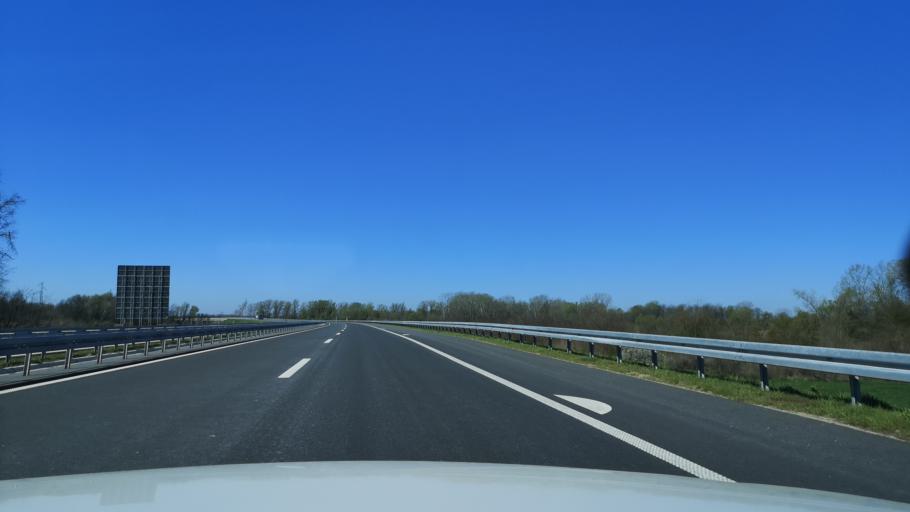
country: RS
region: Central Serbia
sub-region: Belgrade
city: Obrenovac
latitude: 44.6460
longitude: 20.2181
